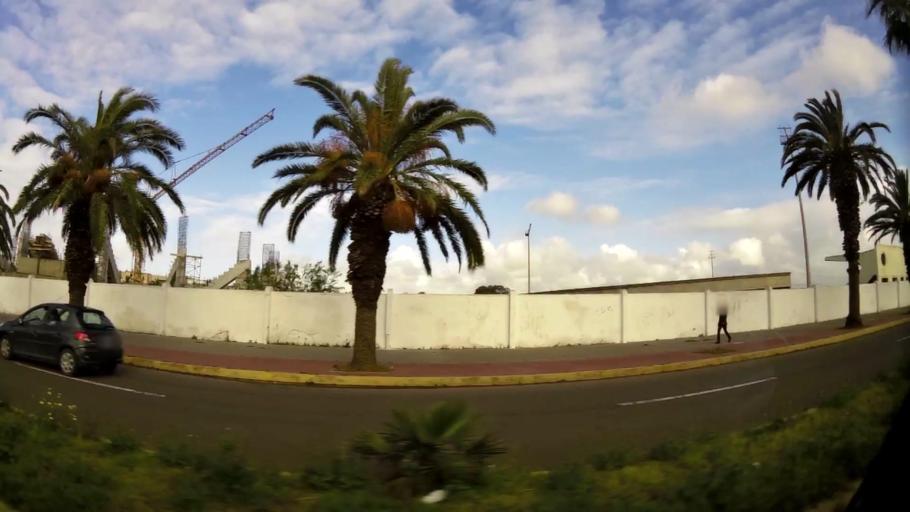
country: MA
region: Grand Casablanca
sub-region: Mohammedia
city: Mohammedia
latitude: 33.6968
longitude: -7.4002
